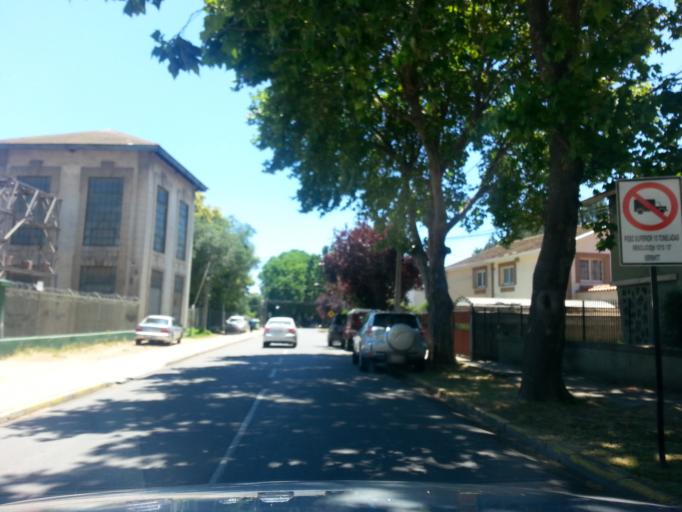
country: CL
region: Valparaiso
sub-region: Provincia de Valparaiso
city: Vina del Mar
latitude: -33.0344
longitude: -71.5249
